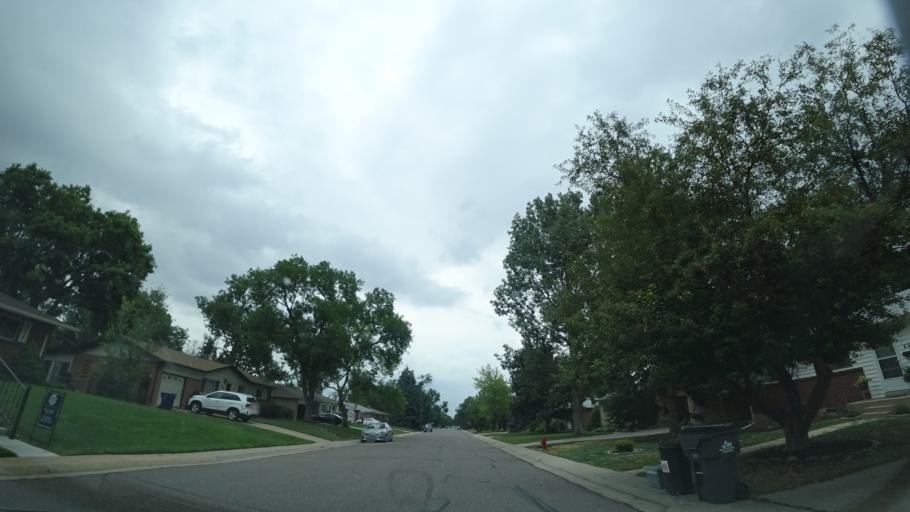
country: US
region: Colorado
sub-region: Jefferson County
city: Lakewood
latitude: 39.7036
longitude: -105.1304
